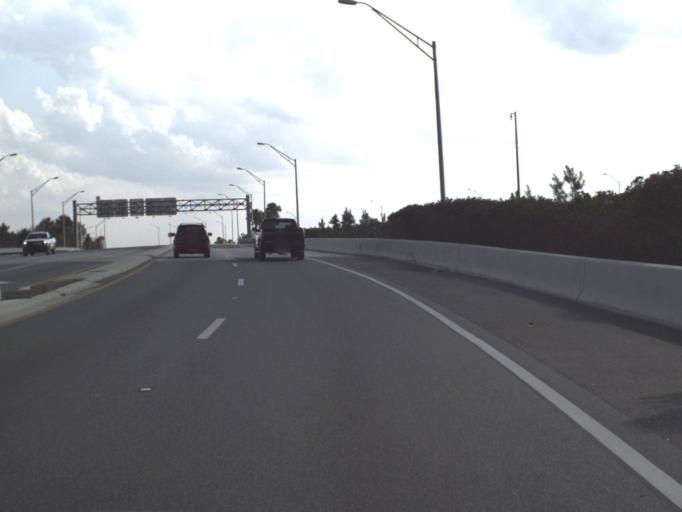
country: US
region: Florida
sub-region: Orange County
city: Apopka
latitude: 28.6826
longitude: -81.5274
